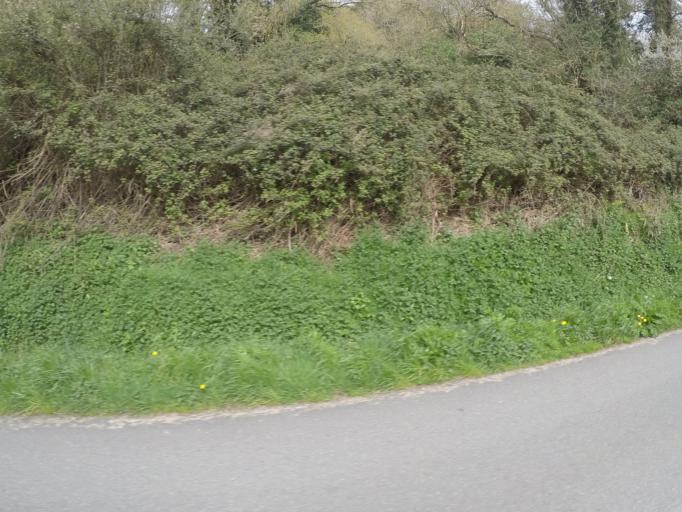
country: FR
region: Brittany
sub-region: Departement des Cotes-d'Armor
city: Plouezec
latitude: 48.7313
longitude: -2.9519
